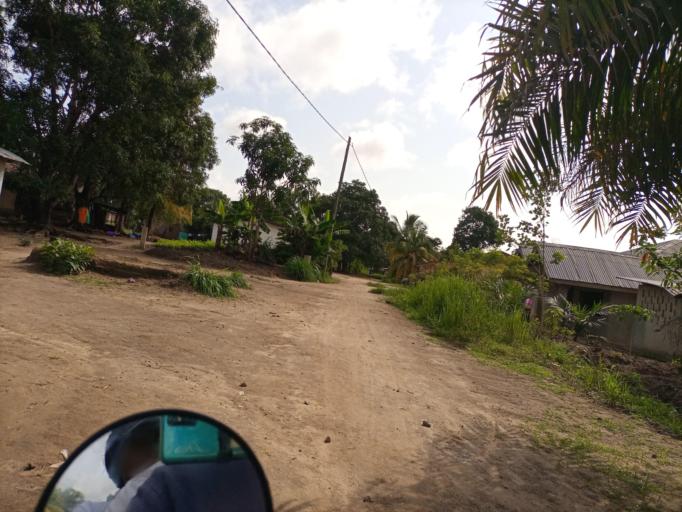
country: SL
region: Southern Province
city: Bo
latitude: 7.9625
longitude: -11.7636
